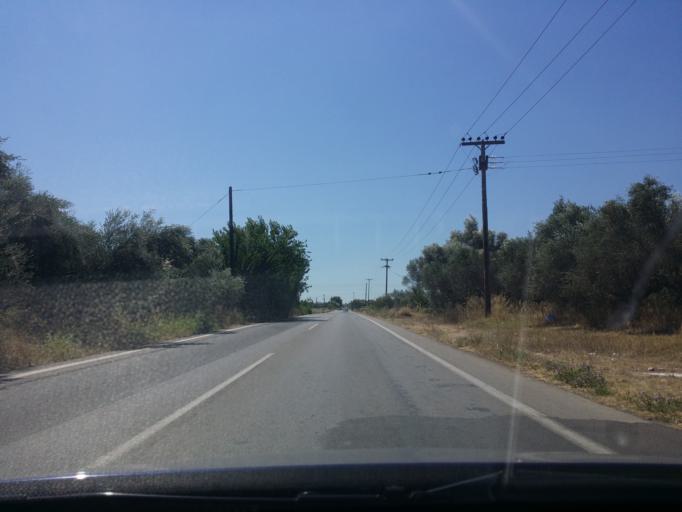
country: GR
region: Peloponnese
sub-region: Nomos Lakonias
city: Sparti
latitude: 37.0058
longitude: 22.4524
